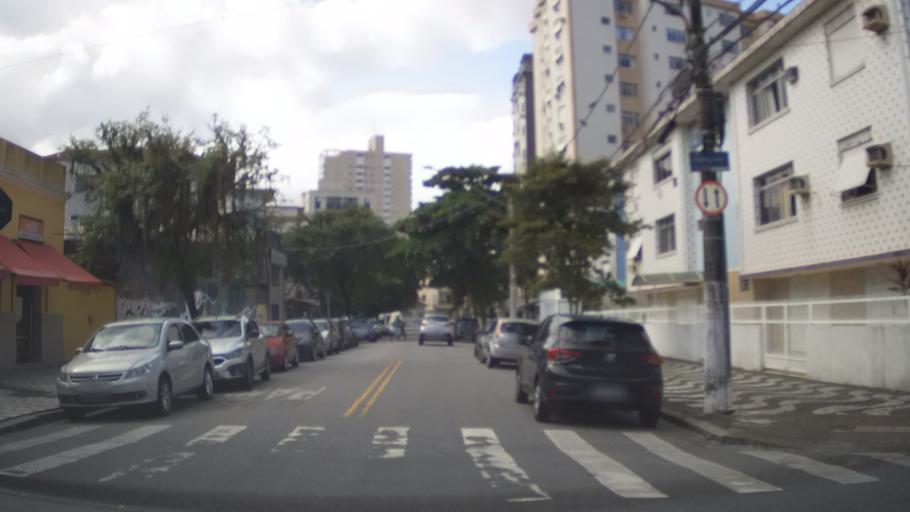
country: BR
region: Sao Paulo
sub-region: Santos
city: Santos
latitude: -23.9557
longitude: -46.3364
